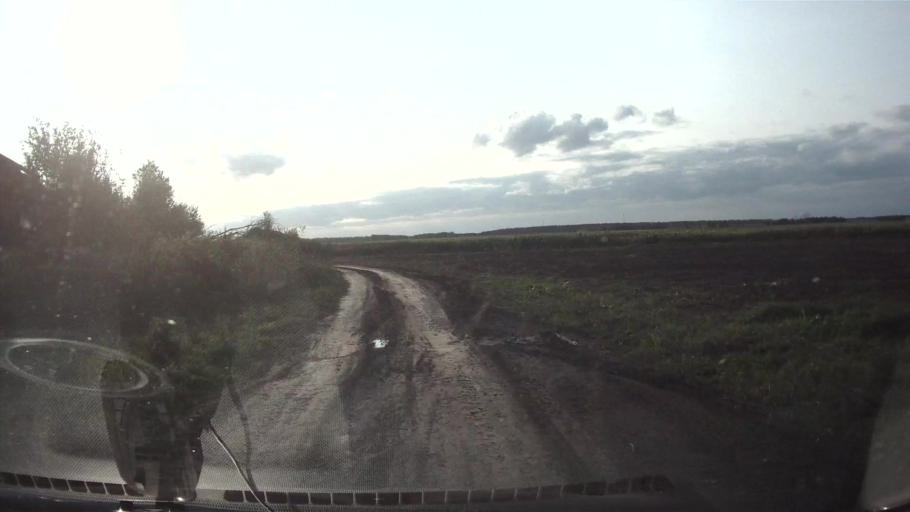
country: RU
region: Mariy-El
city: Kuzhener
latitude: 56.9706
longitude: 48.7873
